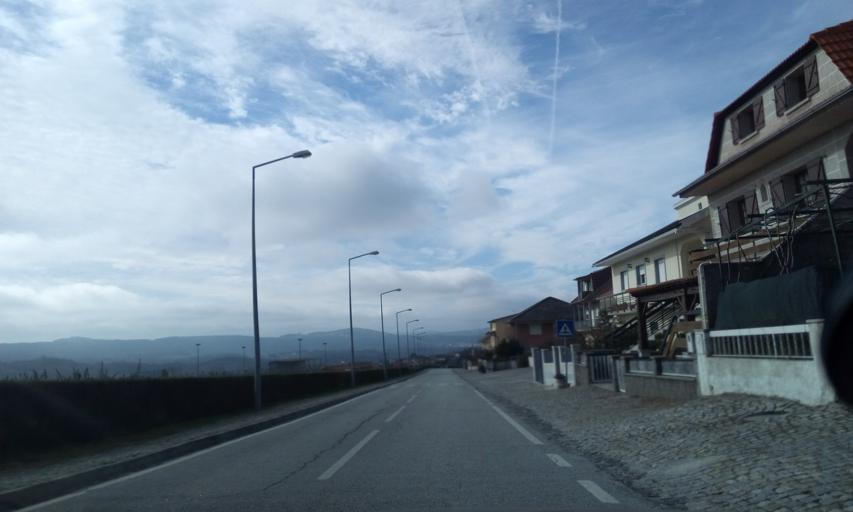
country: PT
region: Guarda
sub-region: Aguiar da Beira
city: Aguiar da Beira
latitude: 40.7388
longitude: -7.5549
